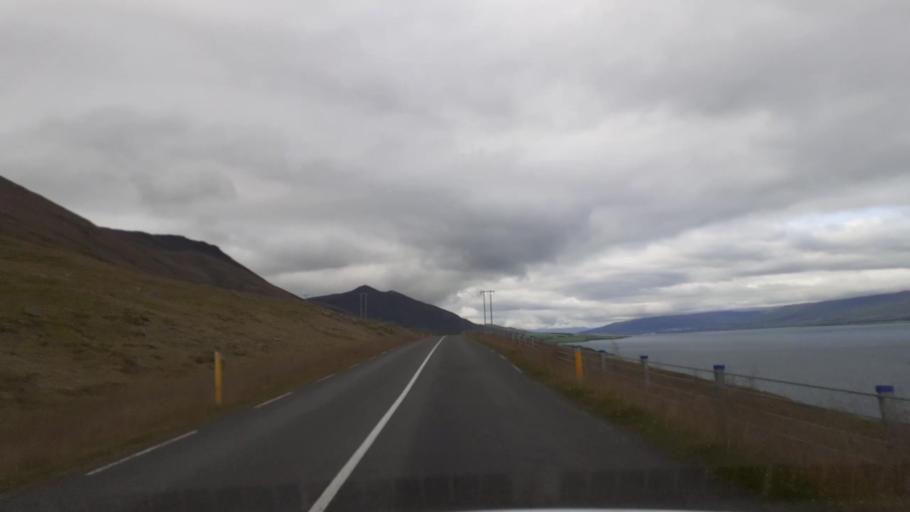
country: IS
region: Northeast
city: Akureyri
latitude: 65.8542
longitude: -18.0614
